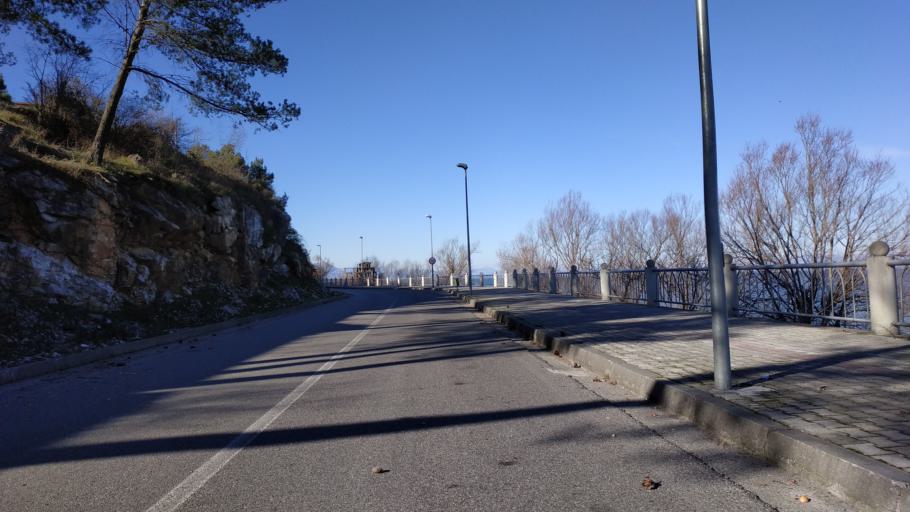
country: AL
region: Shkoder
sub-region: Rrethi i Shkodres
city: Berdica e Madhe
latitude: 42.0571
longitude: 19.4665
